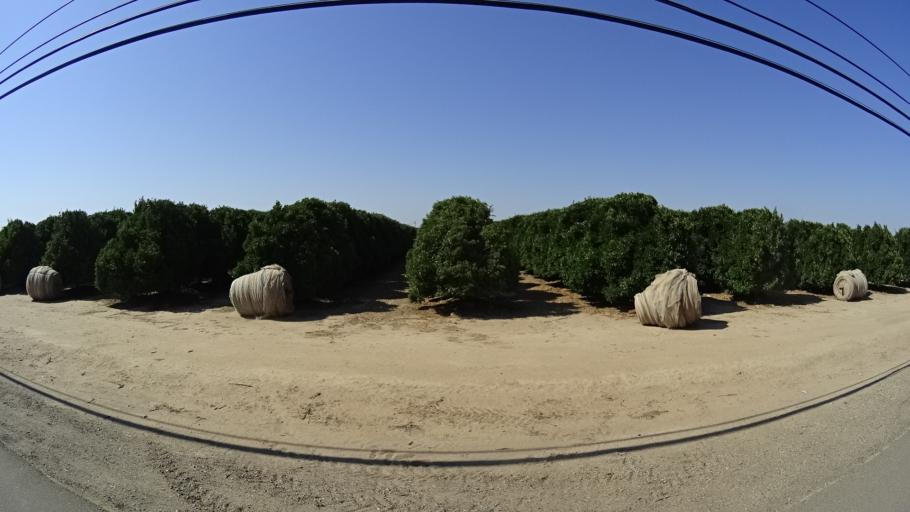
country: US
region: California
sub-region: Fresno County
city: Sunnyside
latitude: 36.7073
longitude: -119.6853
